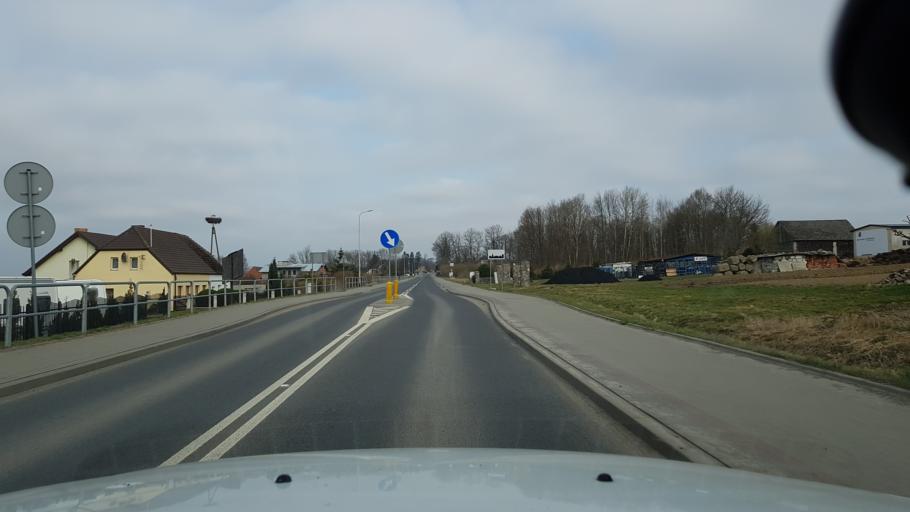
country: PL
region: West Pomeranian Voivodeship
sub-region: Powiat koszalinski
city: Sianow
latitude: 54.2500
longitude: 16.2804
